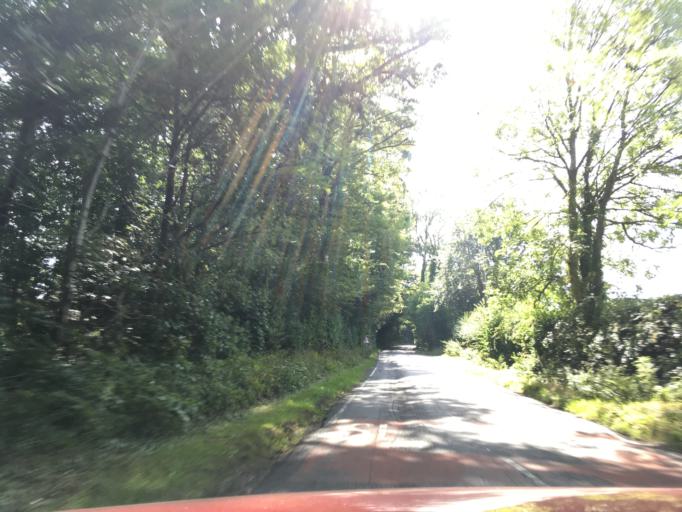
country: GB
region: England
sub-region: Hampshire
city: Highclere
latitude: 51.3562
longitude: -1.3863
